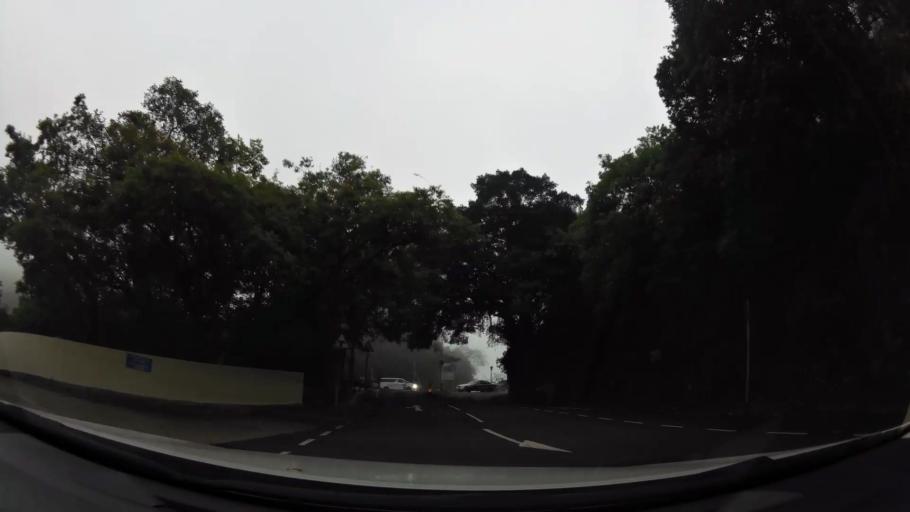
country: HK
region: Wanchai
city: Wan Chai
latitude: 22.2696
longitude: 114.1651
